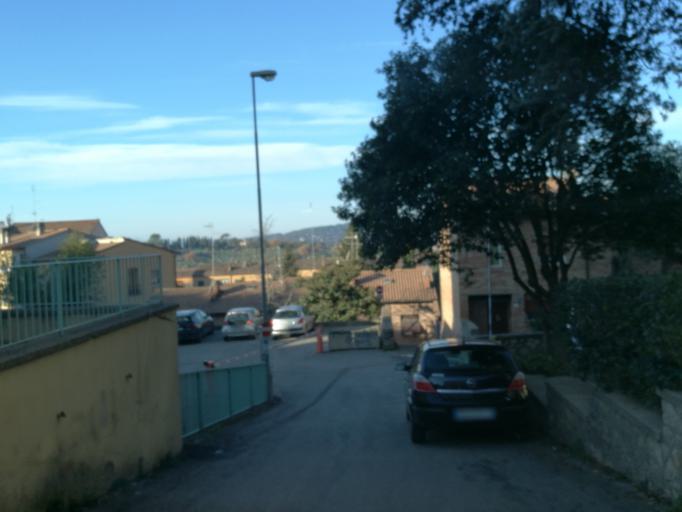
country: IT
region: Umbria
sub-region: Provincia di Perugia
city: Perugia
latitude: 43.0975
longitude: 12.3916
